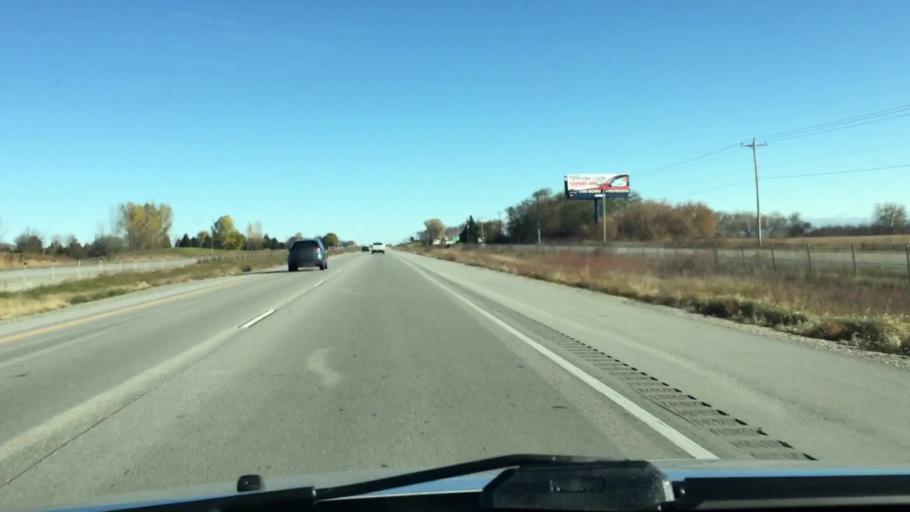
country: US
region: Wisconsin
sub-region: Brown County
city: Wrightstown
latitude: 44.3589
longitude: -88.1847
